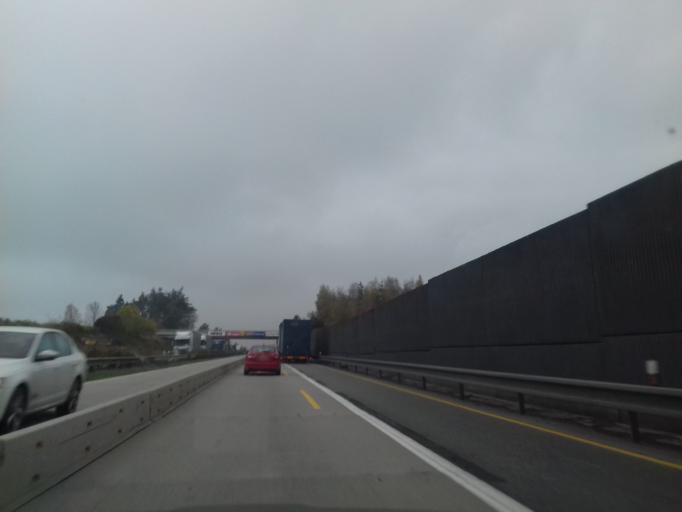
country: CZ
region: Vysocina
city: Velky Beranov
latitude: 49.4334
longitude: 15.6495
